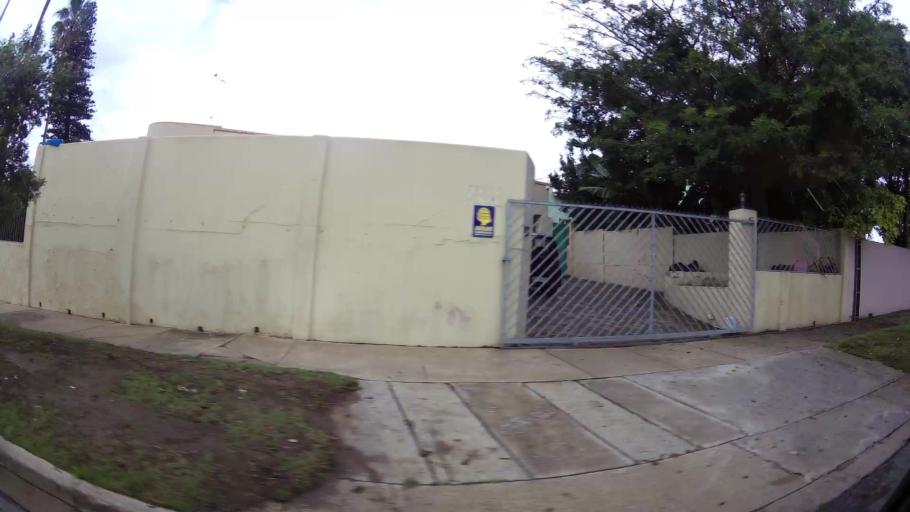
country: ZA
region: Eastern Cape
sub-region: Nelson Mandela Bay Metropolitan Municipality
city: Port Elizabeth
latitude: -33.9543
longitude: 25.5988
